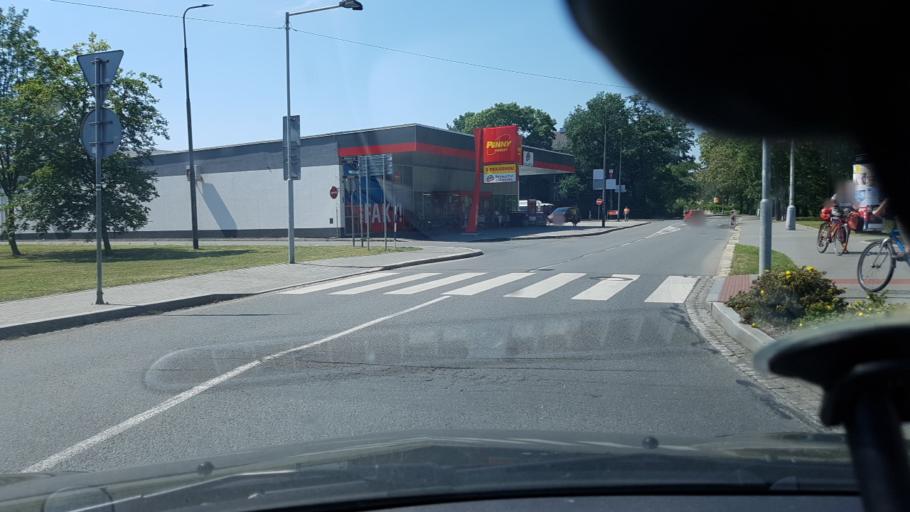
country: CZ
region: Moravskoslezsky
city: Bohumin
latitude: 49.9004
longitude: 18.3545
